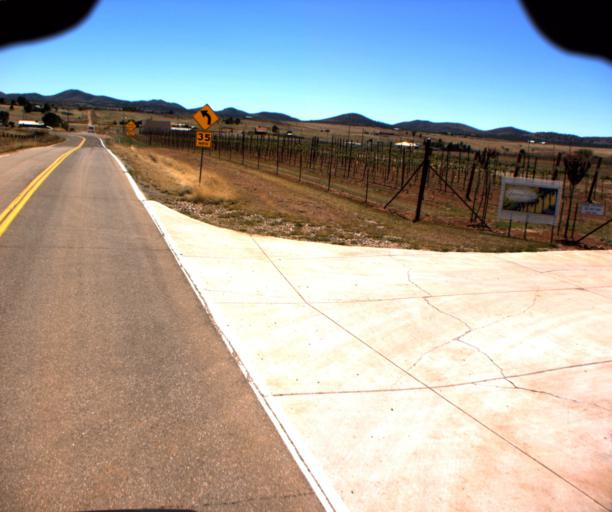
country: US
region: Arizona
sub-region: Cochise County
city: Huachuca City
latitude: 31.6101
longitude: -110.5871
